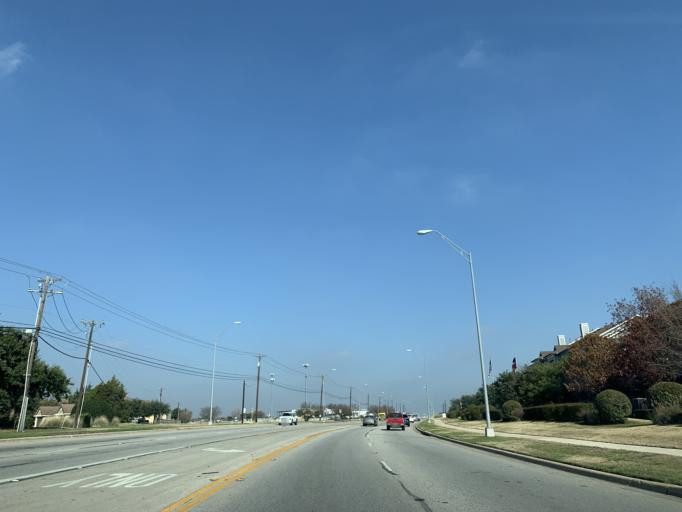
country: US
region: Texas
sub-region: Williamson County
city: Round Rock
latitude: 30.5212
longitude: -97.6555
